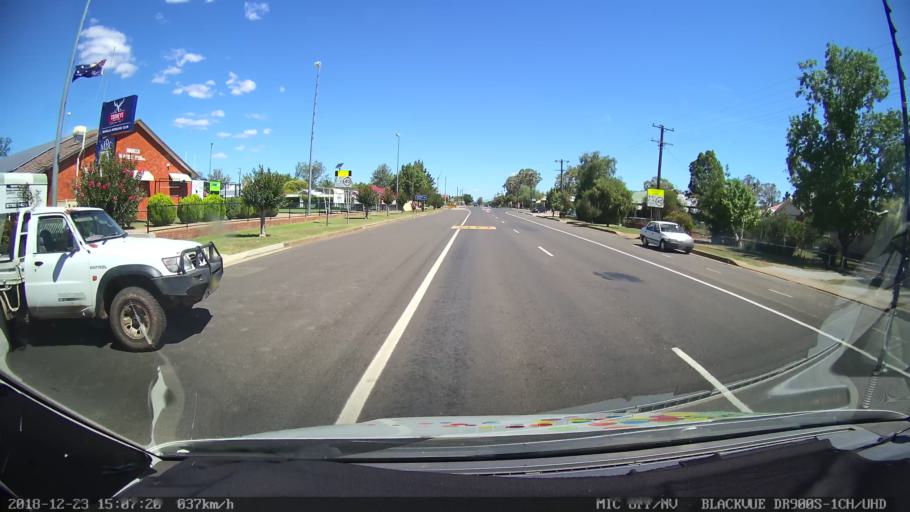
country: AU
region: New South Wales
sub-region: Tamworth Municipality
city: Manilla
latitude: -30.7474
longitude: 150.7243
